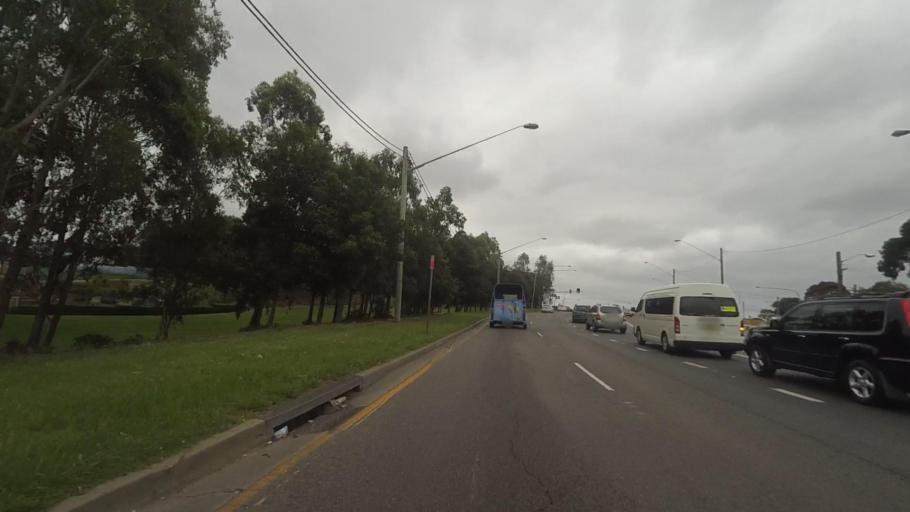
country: AU
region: New South Wales
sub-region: Bankstown
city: Bankstown
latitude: -33.9072
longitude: 151.0402
